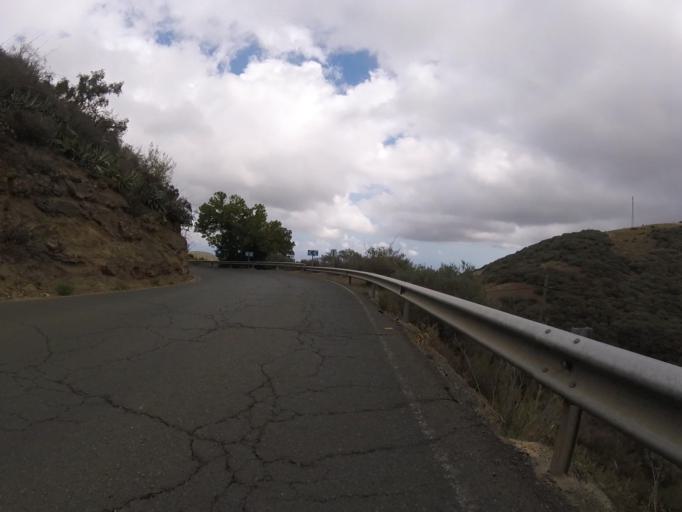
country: ES
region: Canary Islands
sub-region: Provincia de Las Palmas
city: Vega de San Mateo
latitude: 27.9960
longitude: -15.5675
